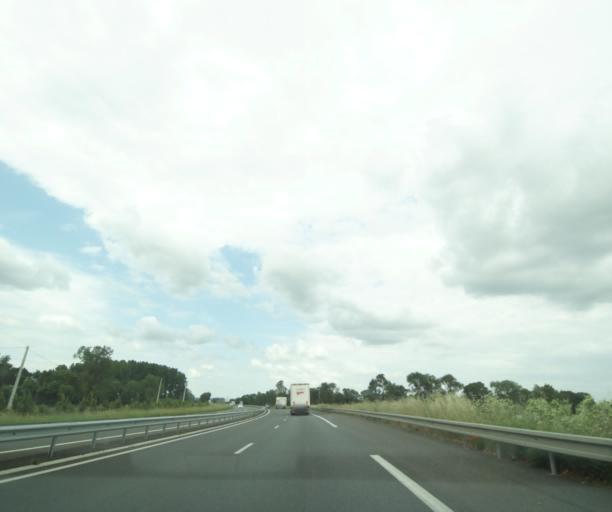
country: FR
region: Pays de la Loire
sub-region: Departement de Maine-et-Loire
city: Villebernier
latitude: 47.2897
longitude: -0.0440
